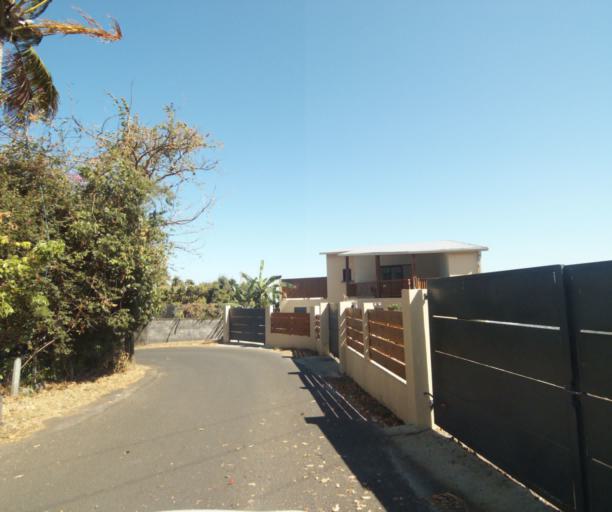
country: RE
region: Reunion
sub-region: Reunion
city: Saint-Paul
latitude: -20.9967
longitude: 55.3270
